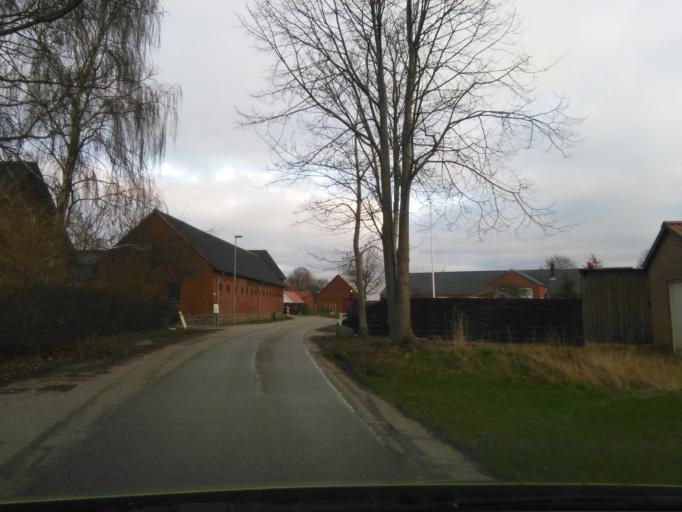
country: DK
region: Central Jutland
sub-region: Arhus Kommune
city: Stavtrup
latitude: 56.1744
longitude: 10.0867
